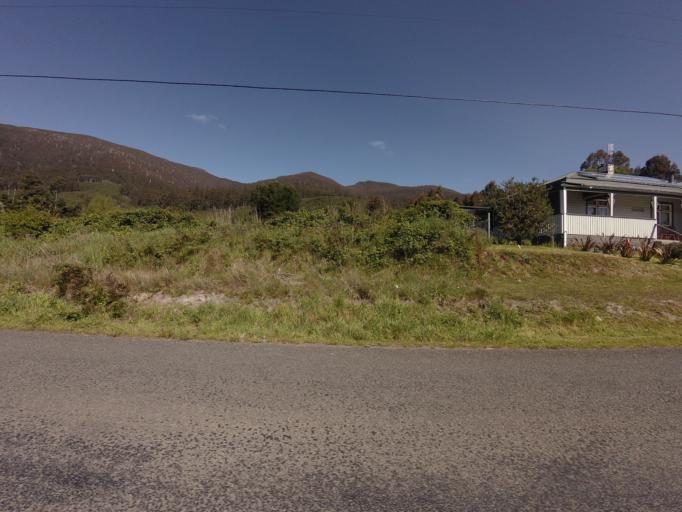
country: AU
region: Tasmania
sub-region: Derwent Valley
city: New Norfolk
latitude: -42.7501
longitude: 146.6434
